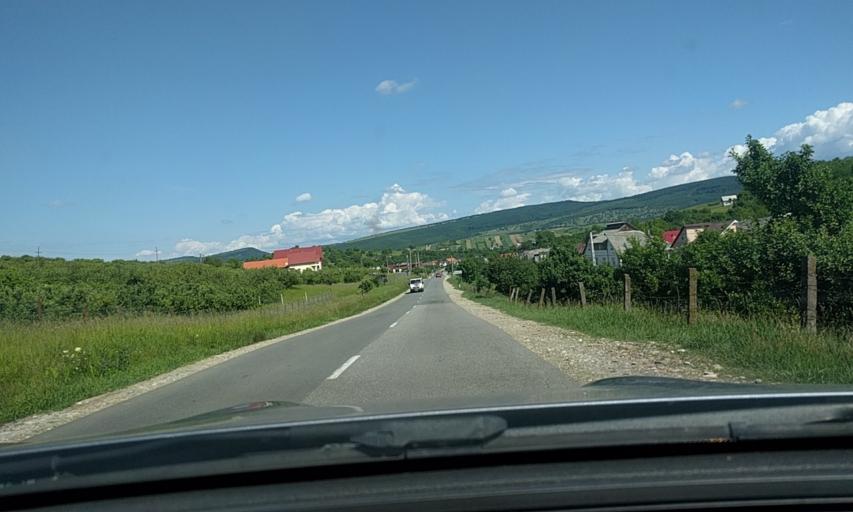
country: RO
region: Bistrita-Nasaud
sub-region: Comuna Dumitra
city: Dumitra
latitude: 47.2109
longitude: 24.4702
